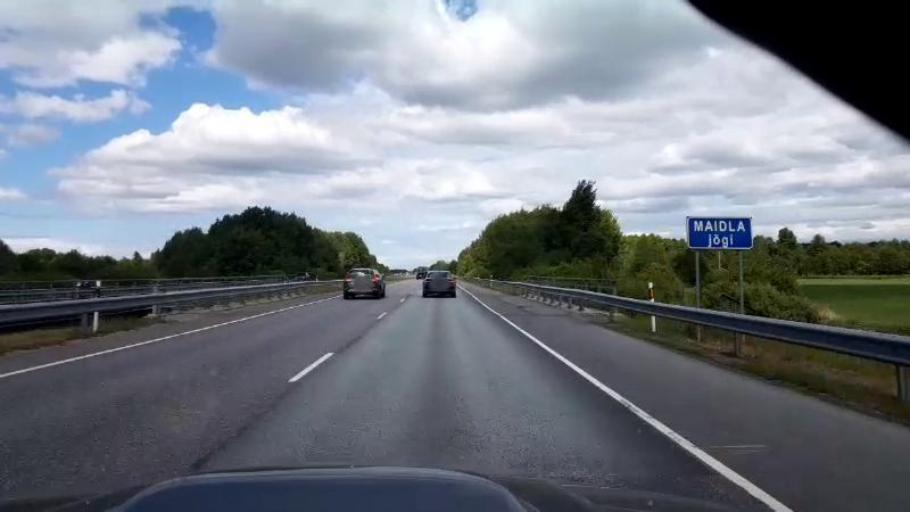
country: EE
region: Harju
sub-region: Saue linn
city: Saue
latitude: 59.2608
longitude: 24.5101
